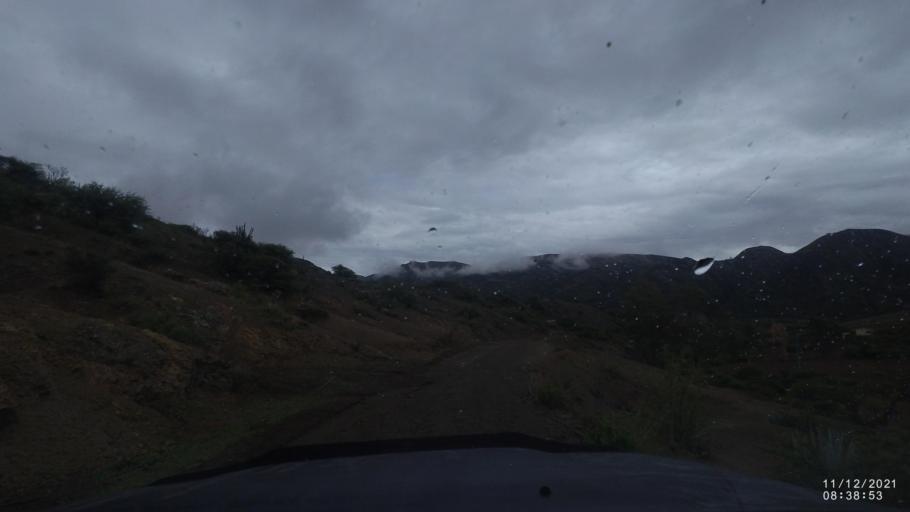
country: BO
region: Cochabamba
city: Tarata
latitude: -17.9227
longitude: -65.9363
